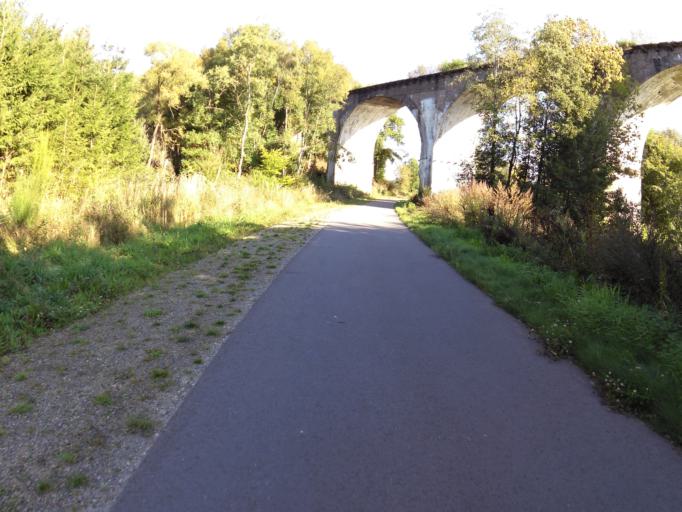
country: BE
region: Wallonia
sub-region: Province de Liege
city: Saint-Vith
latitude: 50.3340
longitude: 6.1173
